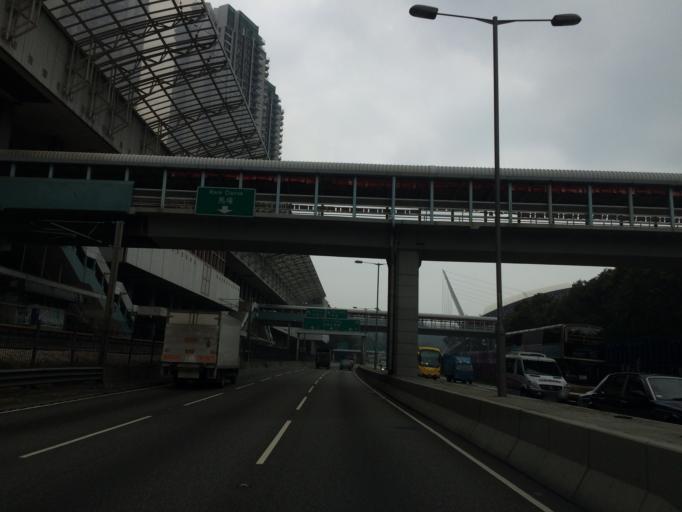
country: HK
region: Sha Tin
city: Sha Tin
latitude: 22.4000
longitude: 114.2027
